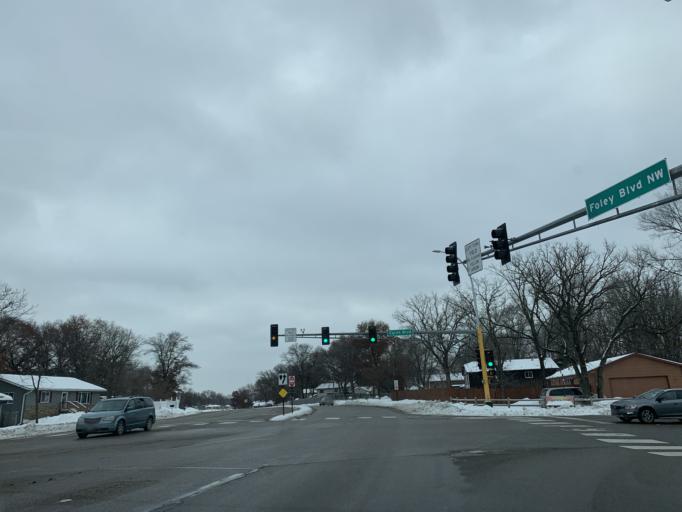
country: US
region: Minnesota
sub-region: Anoka County
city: Blaine
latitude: 45.1642
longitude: -93.2768
